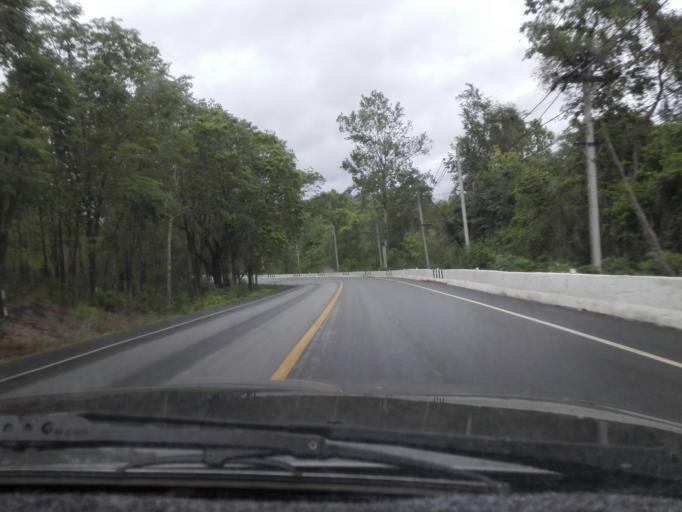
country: TH
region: Tak
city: Tak
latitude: 16.8053
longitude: 98.9968
